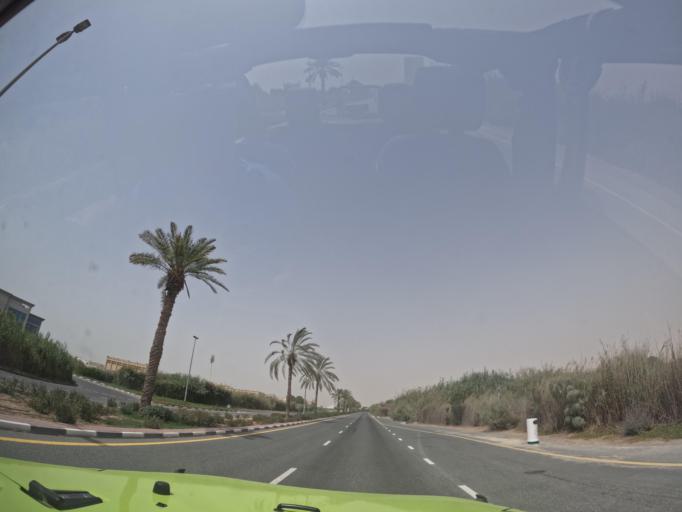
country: AE
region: Dubai
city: Dubai
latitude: 25.1027
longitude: 55.3927
